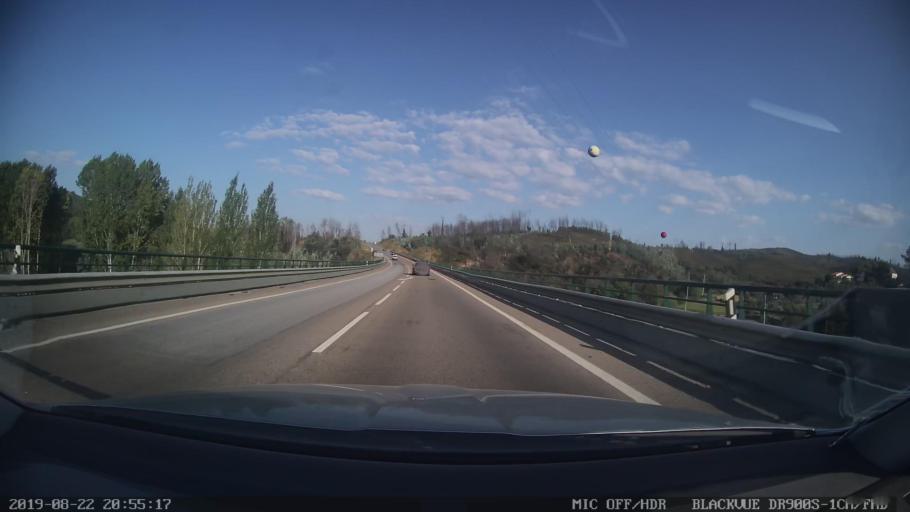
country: PT
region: Castelo Branco
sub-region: Serta
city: Serta
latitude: 39.7791
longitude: -8.0294
